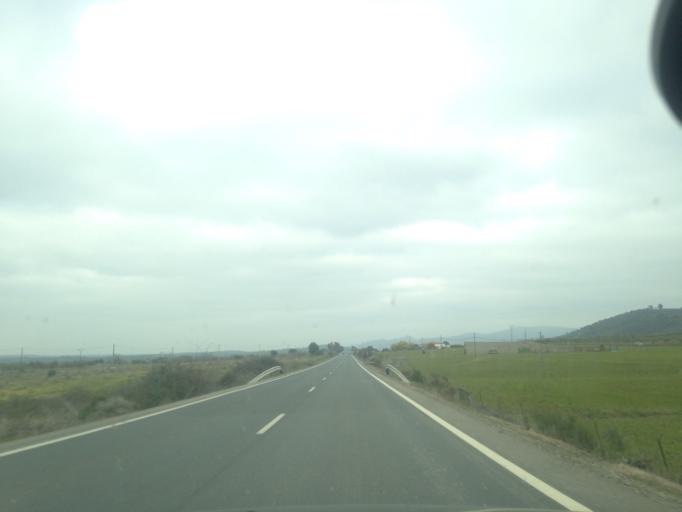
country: ES
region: Extremadura
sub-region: Provincia de Caceres
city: Alcuescar
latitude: 39.1703
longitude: -6.2536
